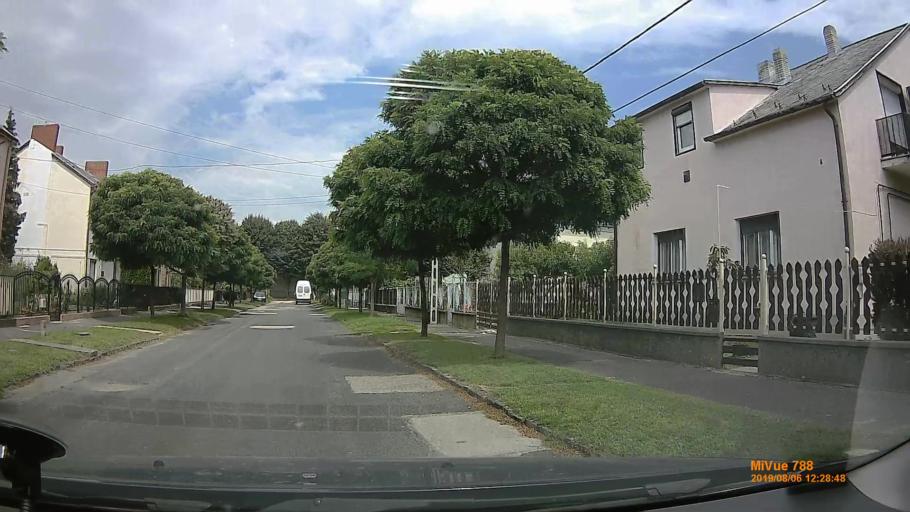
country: HU
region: Zala
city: Nagykanizsa
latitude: 46.4652
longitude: 16.9906
